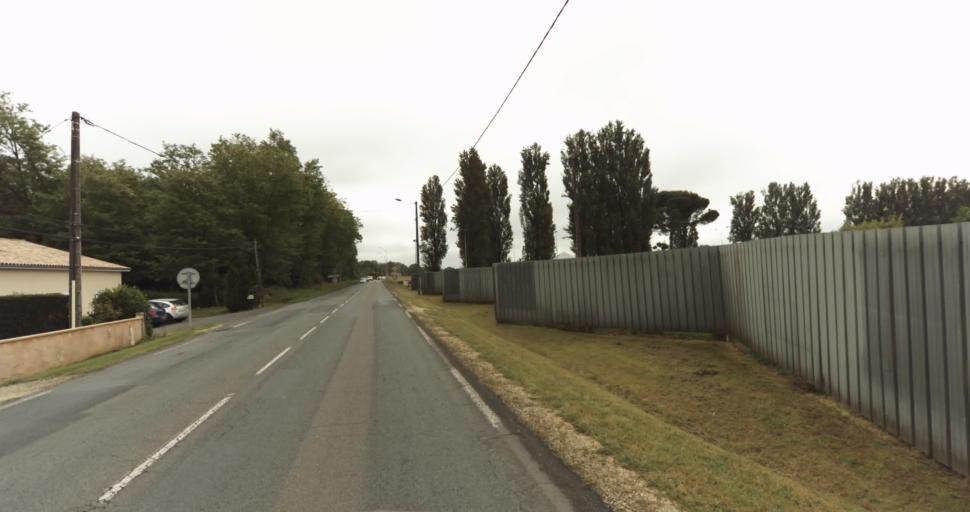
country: FR
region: Aquitaine
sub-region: Departement de la Dordogne
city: Mouleydier
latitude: 44.8525
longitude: 0.6113
